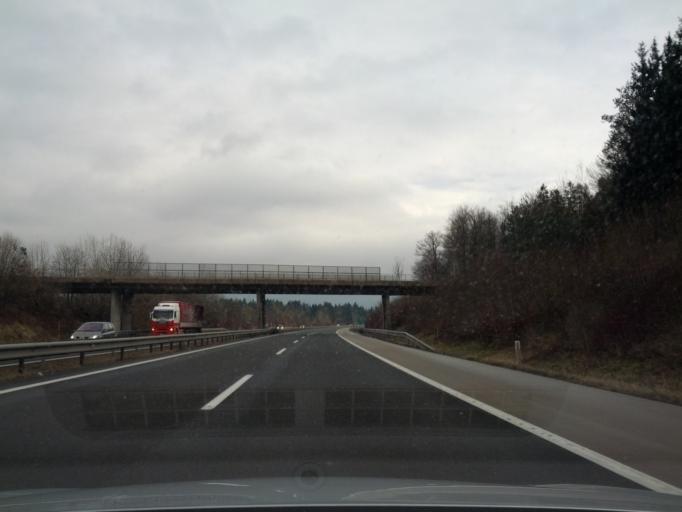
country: SI
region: Kranj
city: Britof
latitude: 46.2536
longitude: 14.3851
